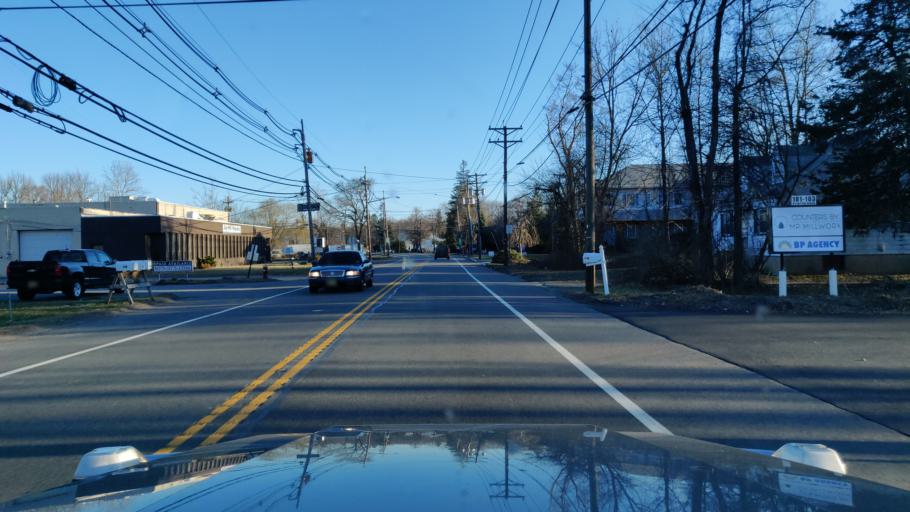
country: US
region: New Jersey
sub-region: Essex County
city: Fairfield
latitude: 40.8643
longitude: -74.3143
